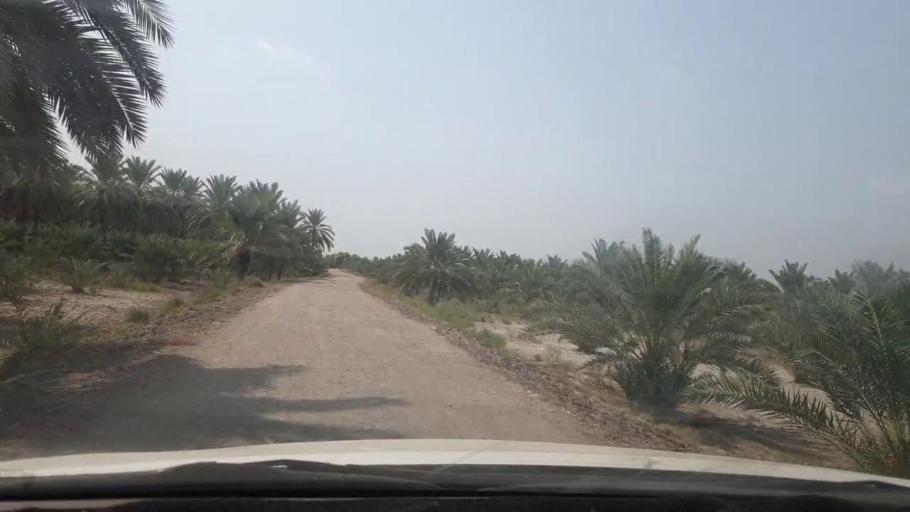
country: PK
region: Sindh
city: Khairpur
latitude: 27.5592
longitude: 68.8509
